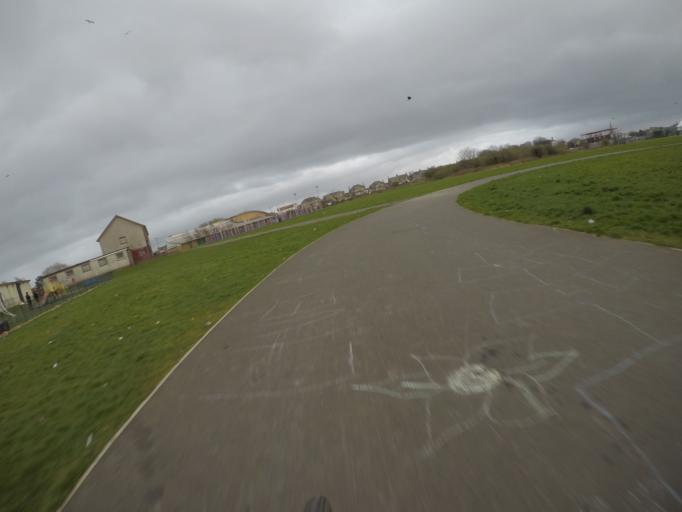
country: GB
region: Scotland
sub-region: North Ayrshire
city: Irvine
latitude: 55.6202
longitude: -4.6612
